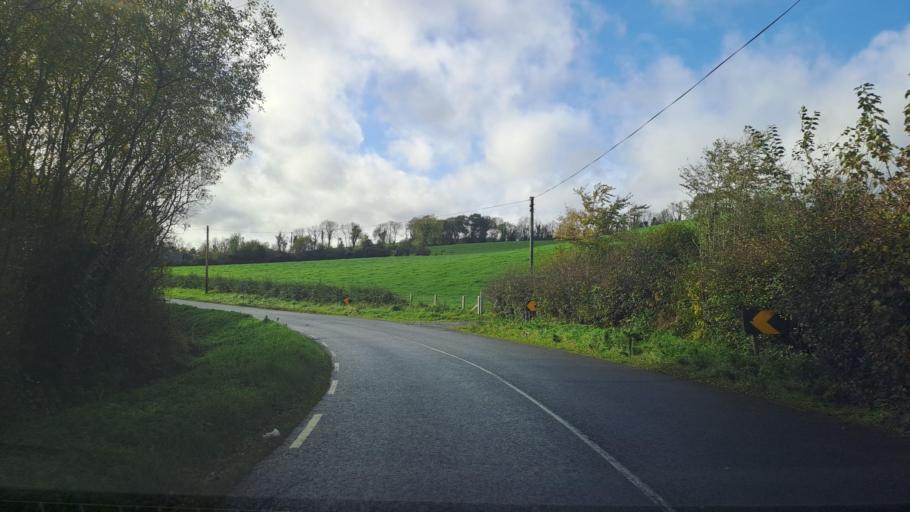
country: IE
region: Ulster
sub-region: County Monaghan
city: Monaghan
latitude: 54.1137
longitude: -6.9461
